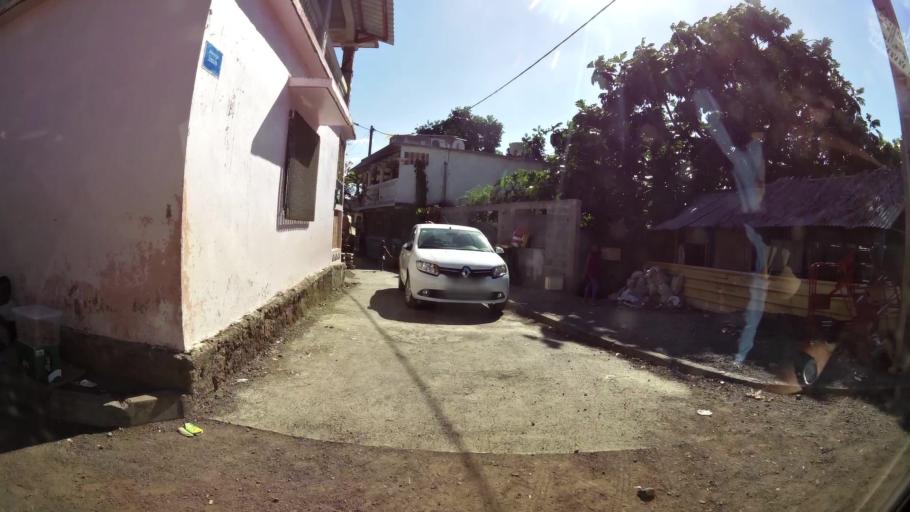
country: YT
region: Pamandzi
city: Pamandzi
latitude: -12.7900
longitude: 45.2722
